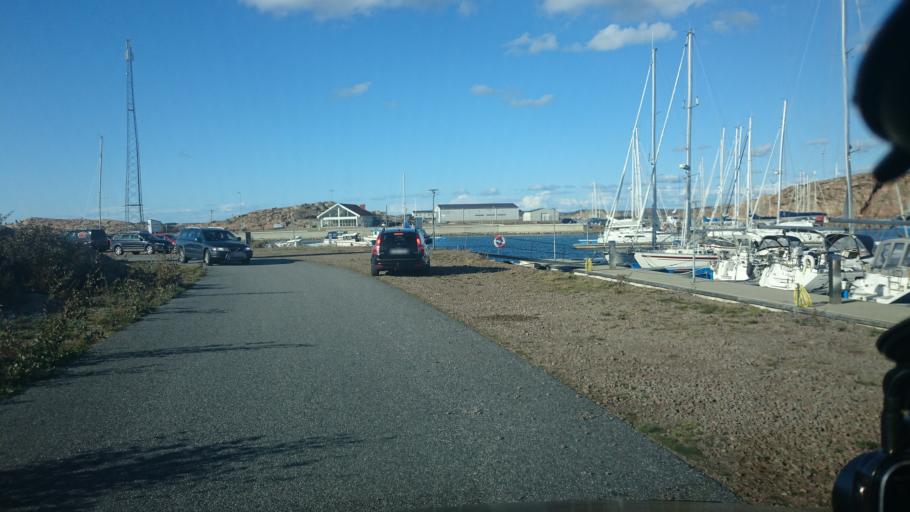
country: SE
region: Vaestra Goetaland
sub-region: Lysekils Kommun
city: Lysekil
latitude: 58.3139
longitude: 11.3962
